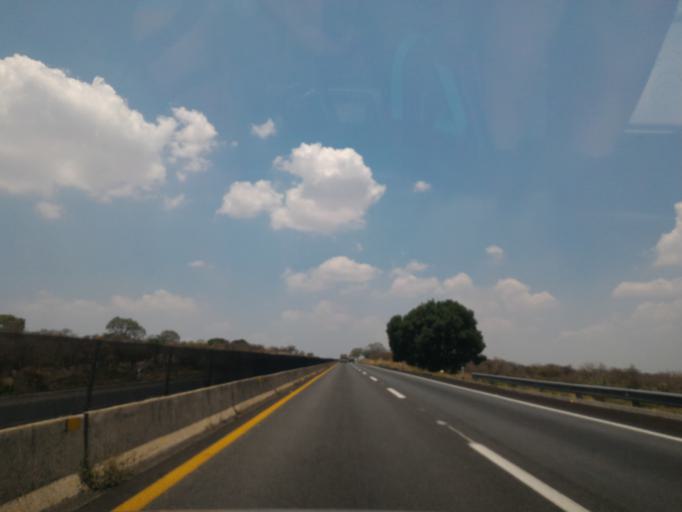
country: MX
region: Jalisco
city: Zapotlanejo
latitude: 20.6838
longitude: -103.0106
